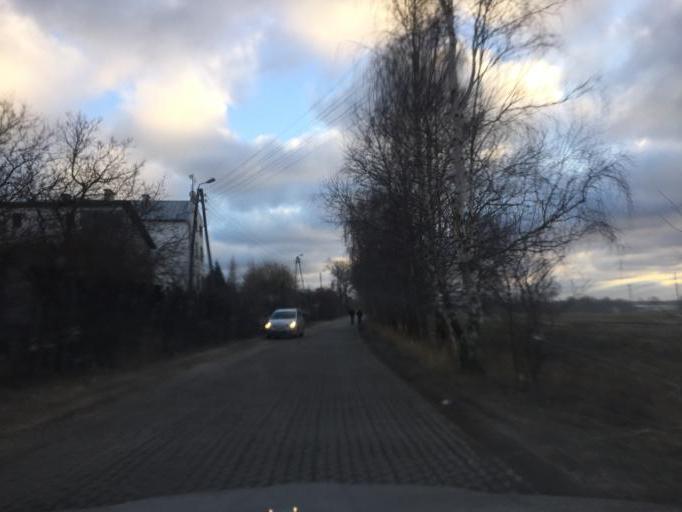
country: PL
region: Pomeranian Voivodeship
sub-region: Powiat kartuski
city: Chwaszczyno
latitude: 54.4127
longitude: 18.4459
